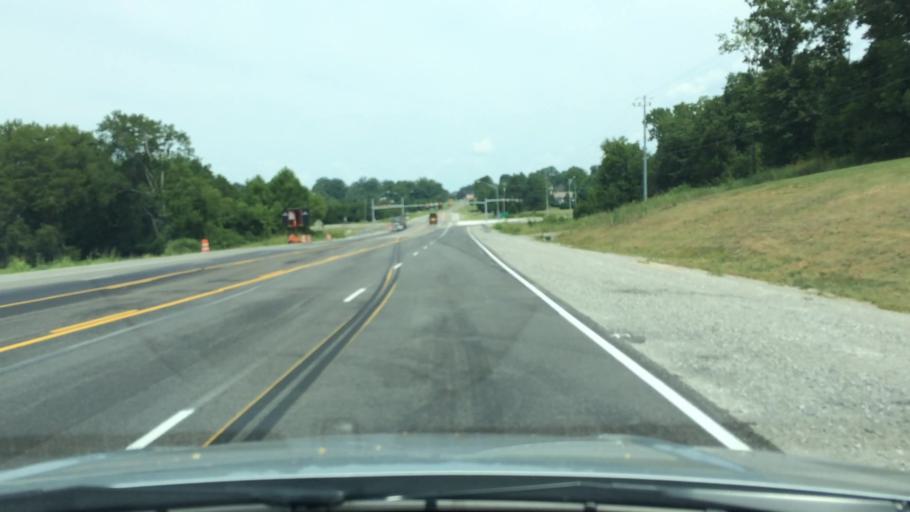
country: US
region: Tennessee
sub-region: Giles County
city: Pulaski
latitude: 35.1678
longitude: -87.0140
